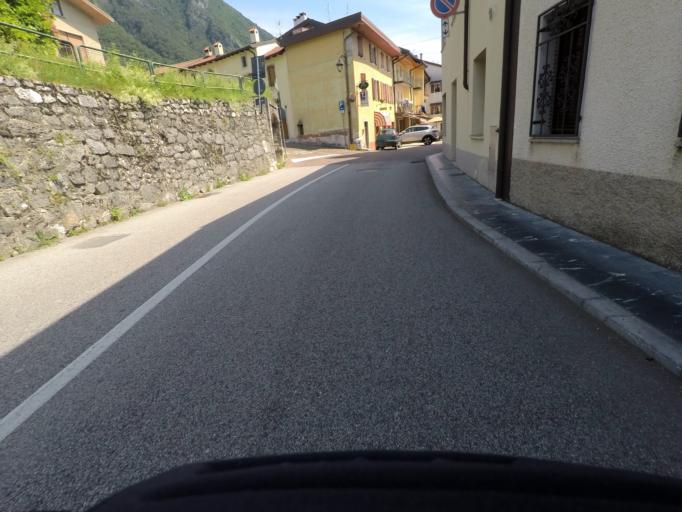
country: IT
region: Friuli Venezia Giulia
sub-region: Provincia di Udine
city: Amaro
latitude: 46.3733
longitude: 13.0939
